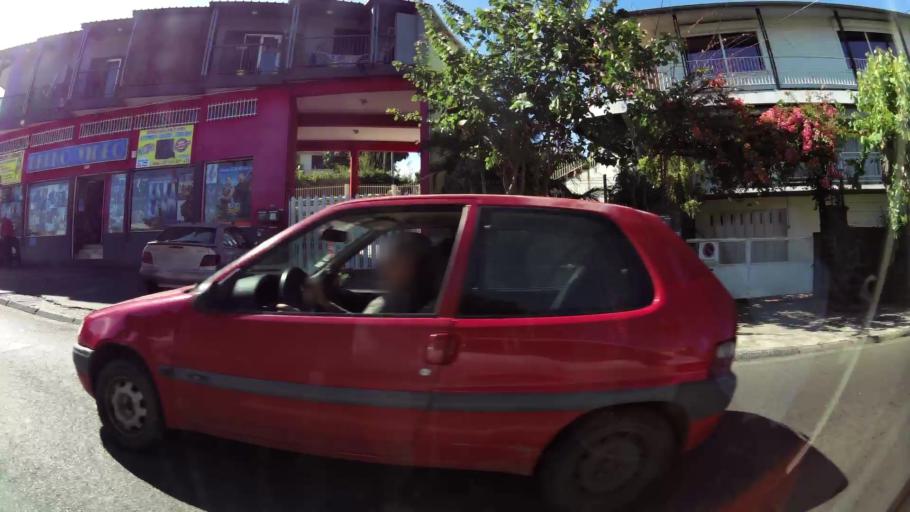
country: RE
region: Reunion
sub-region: Reunion
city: Le Tampon
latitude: -21.2740
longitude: 55.5125
